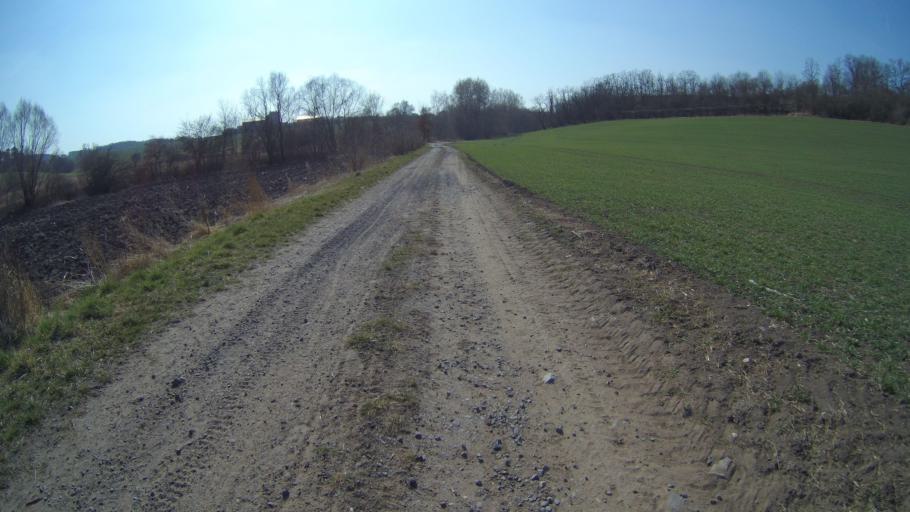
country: CZ
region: Ustecky
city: Mecholupy
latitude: 50.2513
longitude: 13.5254
